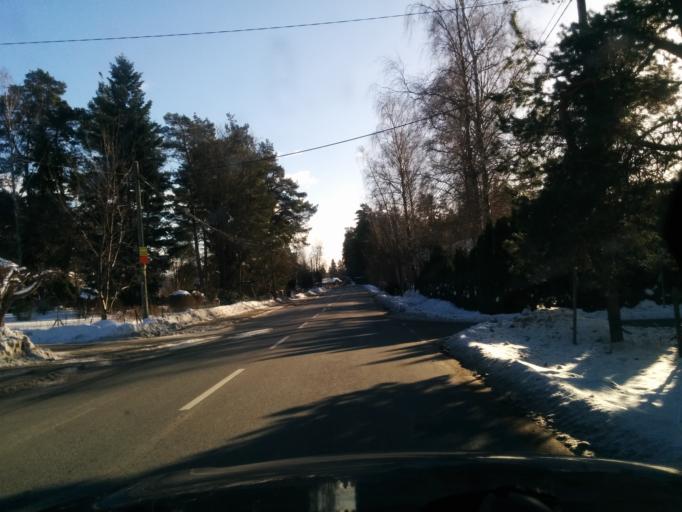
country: SE
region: Stockholm
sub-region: Taby Kommun
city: Taby
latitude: 59.4754
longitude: 18.0956
